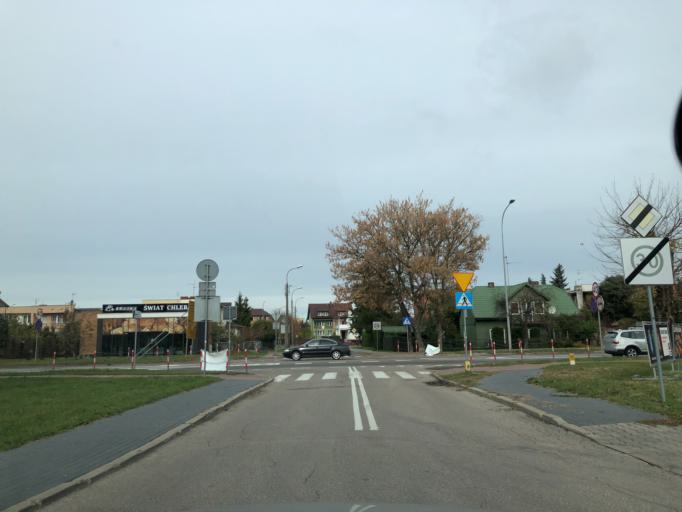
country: PL
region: Podlasie
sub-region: Lomza
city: Lomza
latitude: 53.1781
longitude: 22.0615
